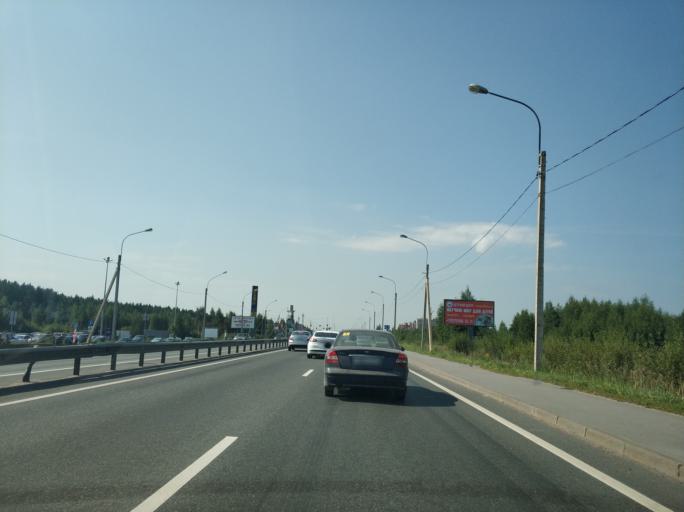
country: RU
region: Leningrad
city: Vsevolozhsk
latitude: 60.0282
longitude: 30.6193
